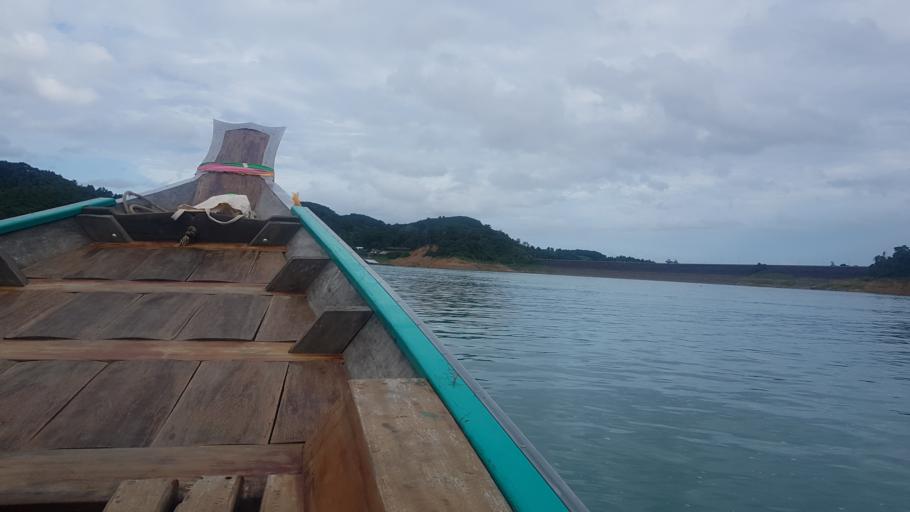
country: TH
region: Surat Thani
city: Ban Takhun
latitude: 8.9777
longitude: 98.8154
